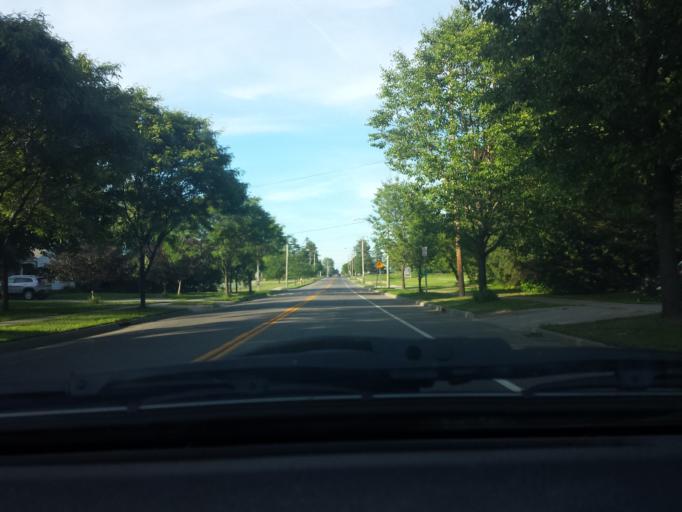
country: US
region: New York
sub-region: St. Lawrence County
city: Potsdam
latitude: 44.6742
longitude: -74.9757
